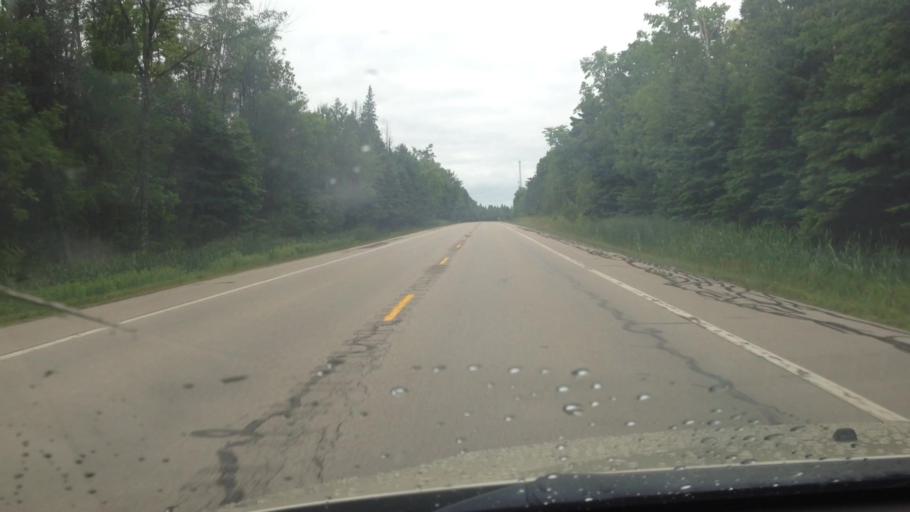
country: US
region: Michigan
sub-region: Menominee County
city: Menominee
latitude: 45.3990
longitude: -87.3652
